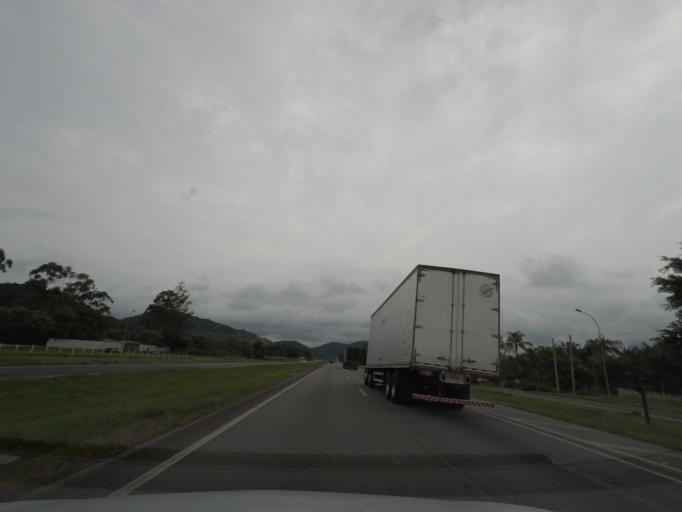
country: BR
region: Sao Paulo
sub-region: Juquia
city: Juquia
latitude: -24.3404
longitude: -47.6454
